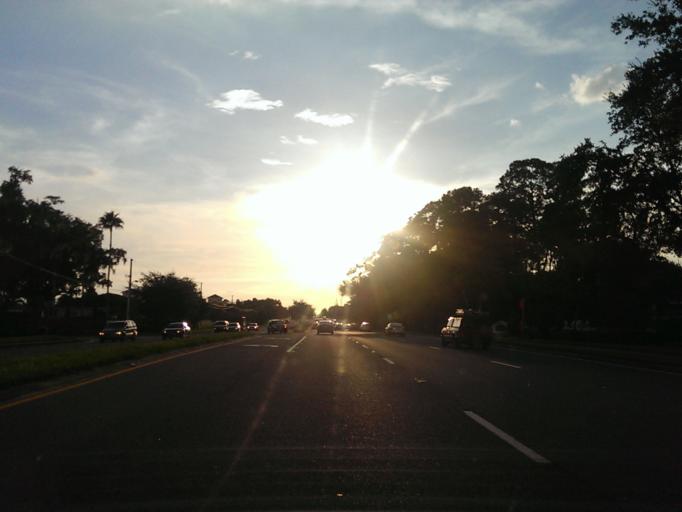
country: US
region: Florida
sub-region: Orange County
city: Tangelo Park
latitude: 28.4938
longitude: -81.4704
